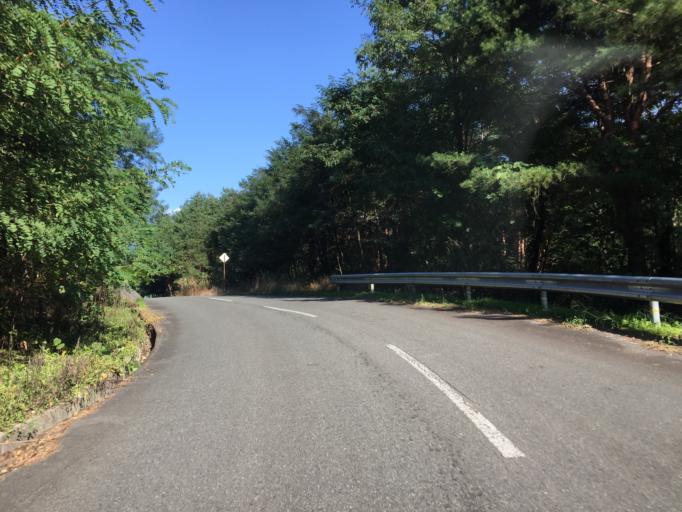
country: JP
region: Yamagata
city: Yonezawa
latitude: 37.8655
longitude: 140.1762
